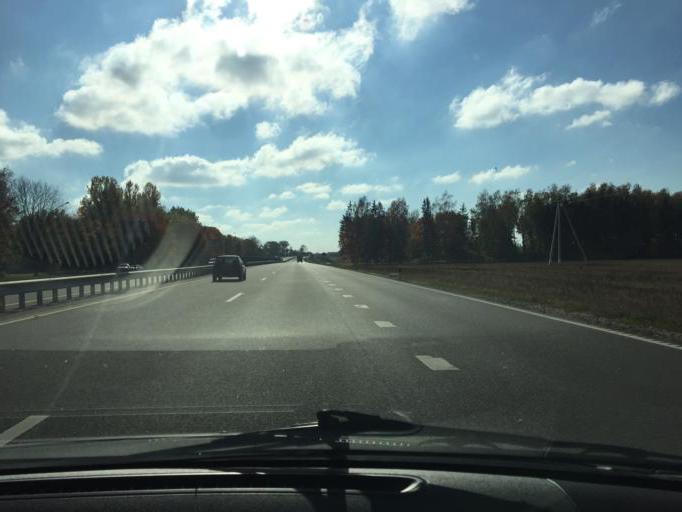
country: BY
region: Minsk
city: Slutsk
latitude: 53.0909
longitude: 27.5699
